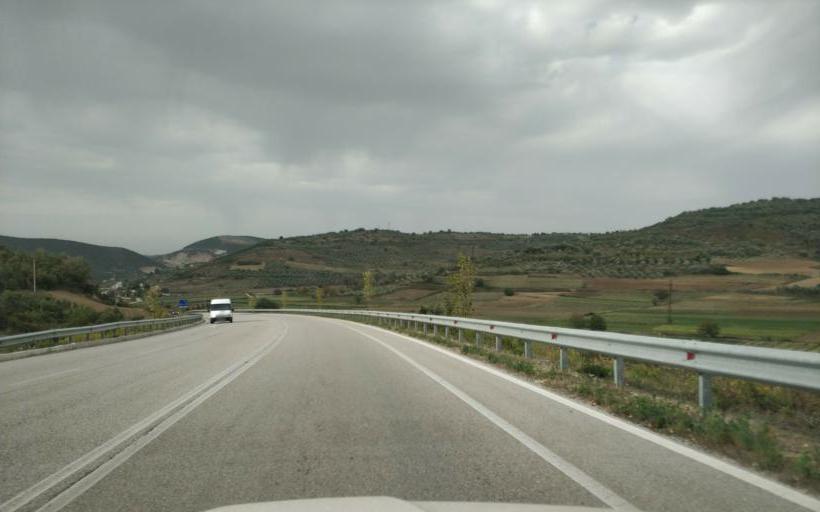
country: AL
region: Fier
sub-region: Rrethi i Mallakastres
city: Fratar
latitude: 40.4942
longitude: 19.8295
